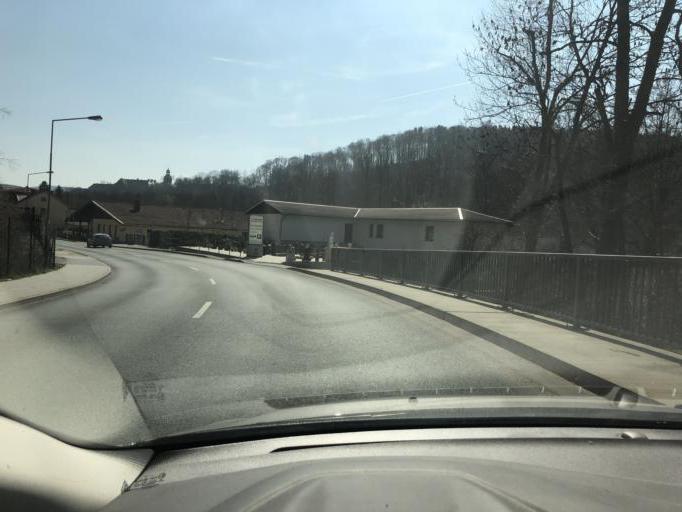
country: DE
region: Thuringia
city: Rudolstadt
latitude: 50.7307
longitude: 11.3336
